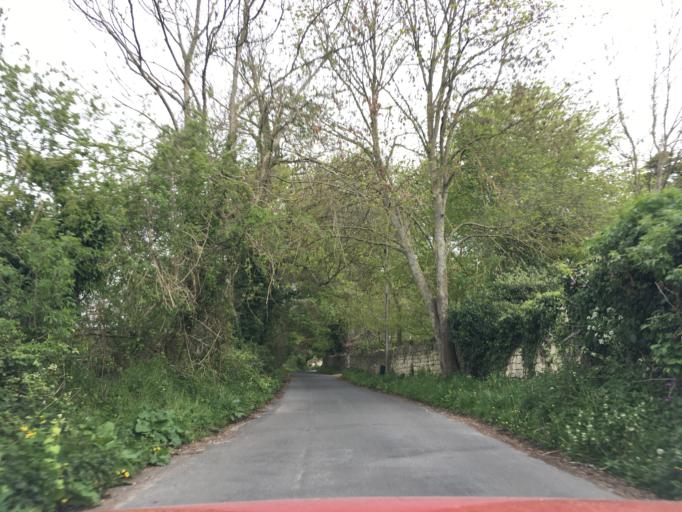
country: GB
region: England
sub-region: Bath and North East Somerset
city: Bath
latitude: 51.3559
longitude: -2.3391
